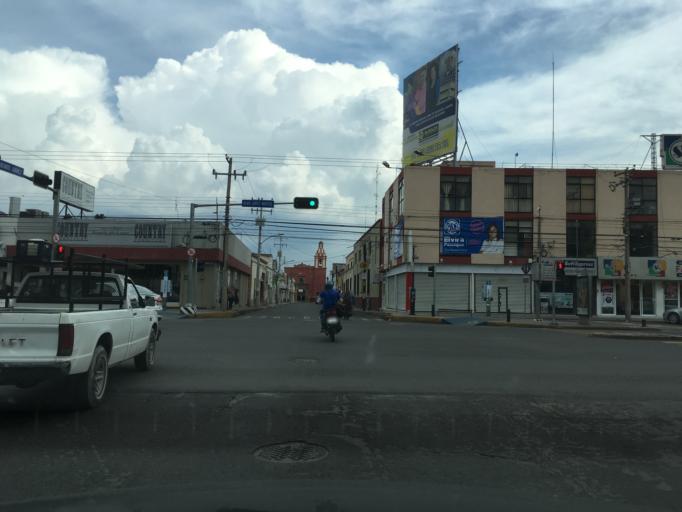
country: MX
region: Guanajuato
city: Celaya
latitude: 20.5199
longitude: -100.8154
